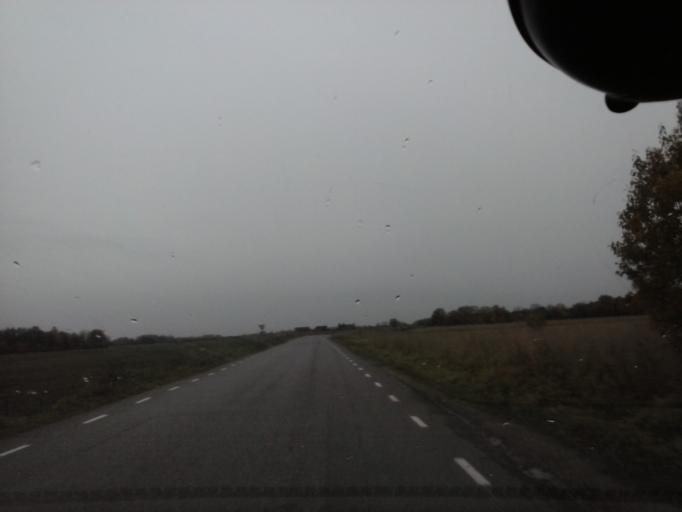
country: EE
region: Viljandimaa
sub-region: Vohma linn
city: Vohma
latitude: 58.6832
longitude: 25.6818
